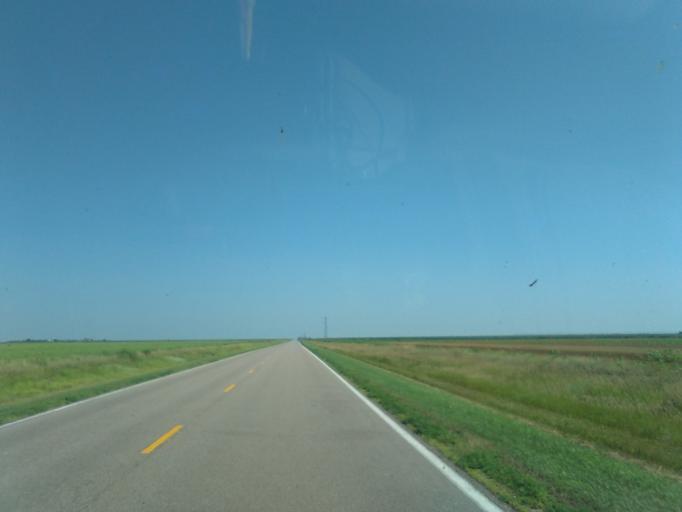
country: US
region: Kansas
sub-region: Cheyenne County
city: Saint Francis
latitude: 39.7622
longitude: -101.5421
